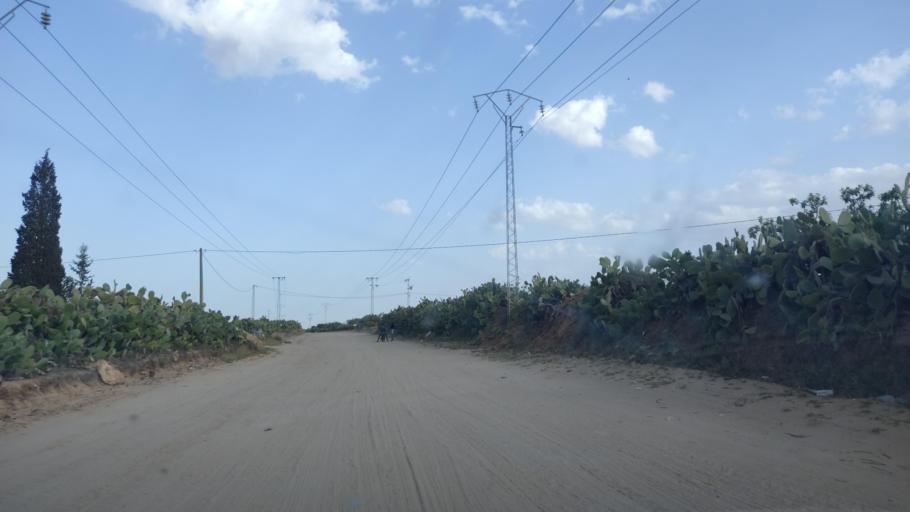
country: TN
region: Safaqis
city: Sfax
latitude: 34.8569
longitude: 10.6046
